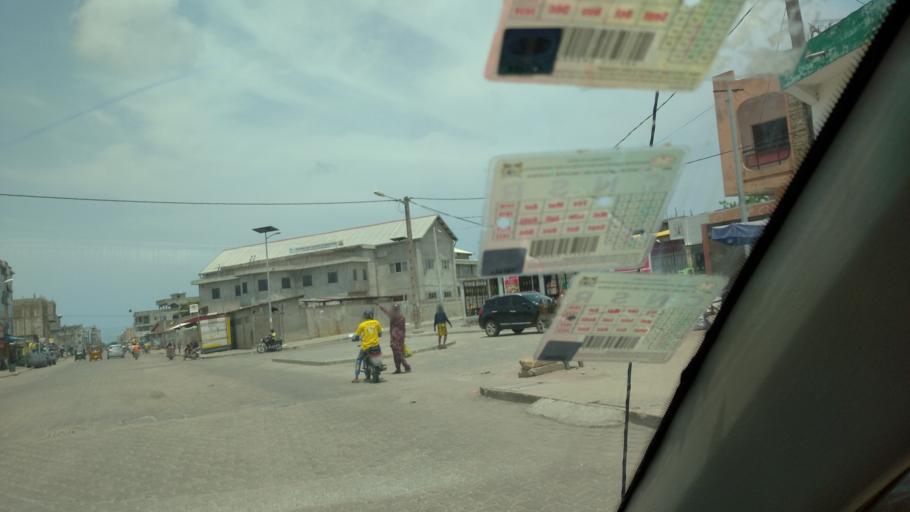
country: BJ
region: Littoral
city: Cotonou
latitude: 6.3930
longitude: 2.4499
